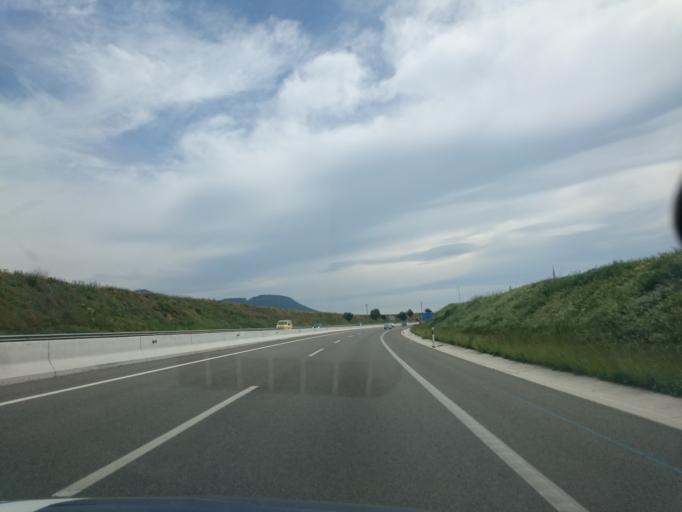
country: ES
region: Catalonia
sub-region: Provincia de Barcelona
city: Artes
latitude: 41.7941
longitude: 1.9186
